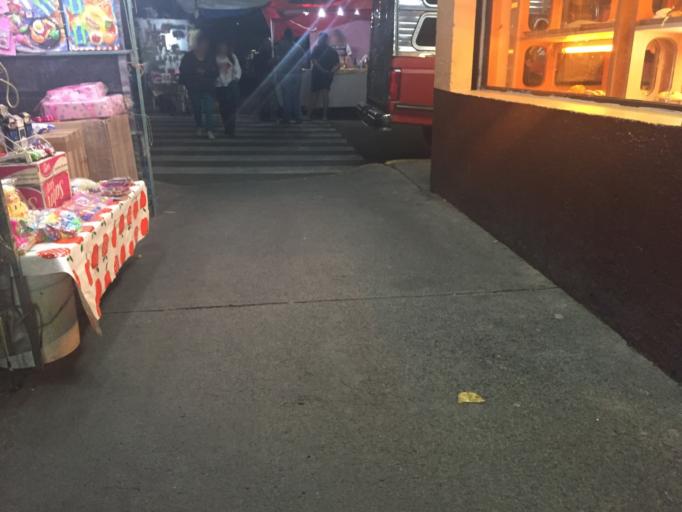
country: MX
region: Mexico City
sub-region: Iztacalco
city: Iztacalco
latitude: 19.3935
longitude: -99.0666
